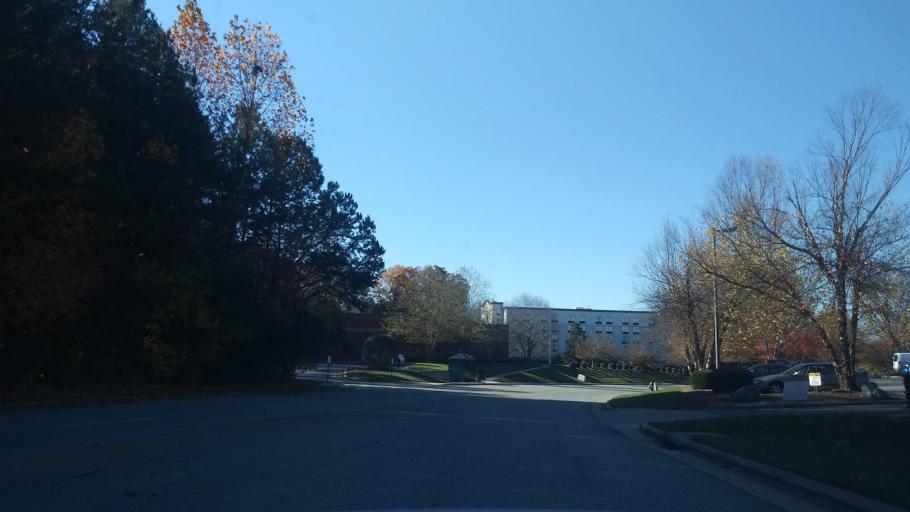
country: US
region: North Carolina
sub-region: Guilford County
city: Jamestown
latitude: 36.0516
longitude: -79.8911
